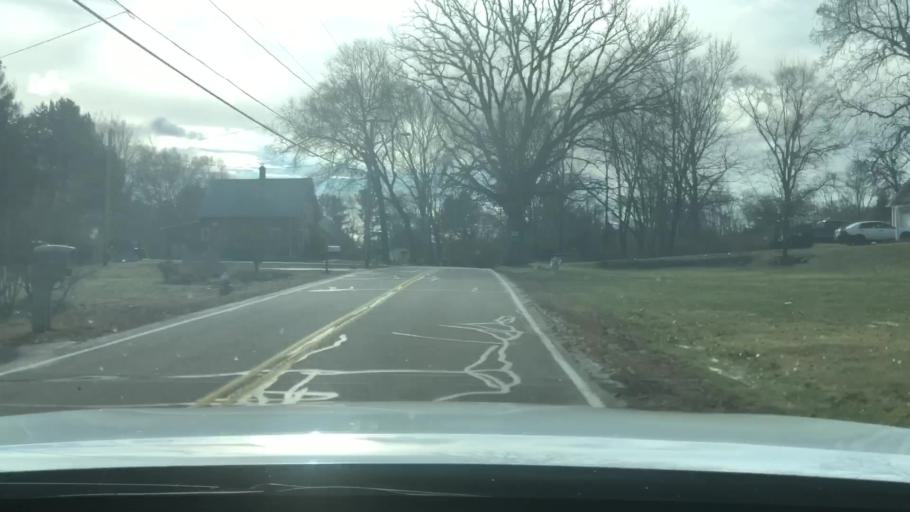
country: US
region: Massachusetts
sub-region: Worcester County
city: Blackstone
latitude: 42.0307
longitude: -71.5246
